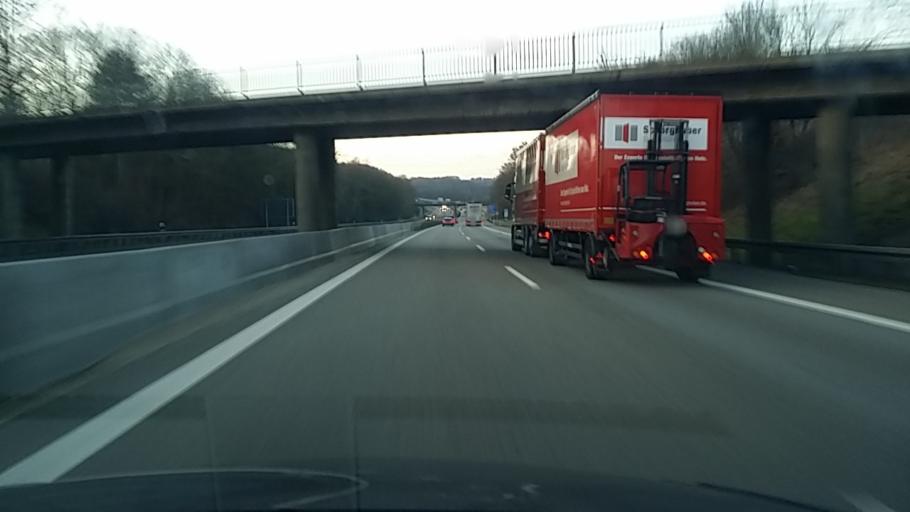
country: DE
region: Bavaria
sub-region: Upper Palatinate
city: Nittendorf
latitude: 49.0253
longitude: 11.9564
